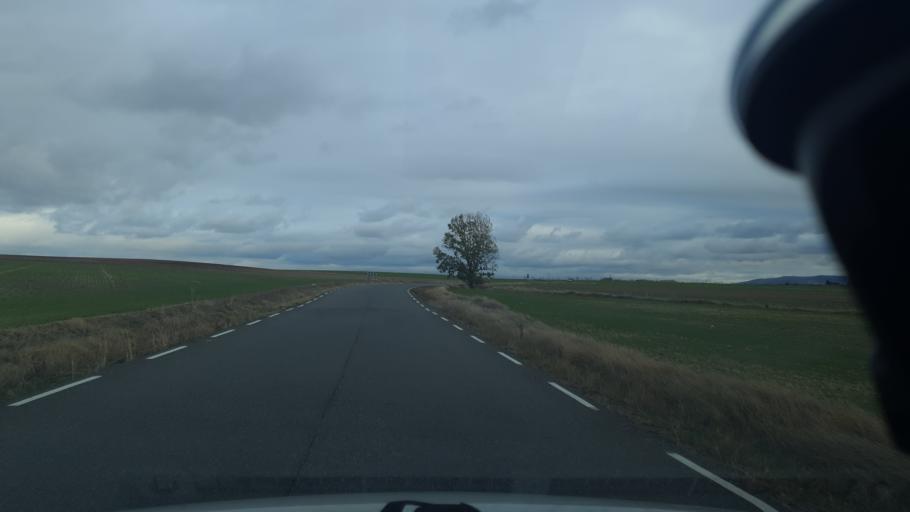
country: ES
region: Castille and Leon
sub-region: Provincia de Avila
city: Velayos
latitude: 40.8354
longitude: -4.6158
